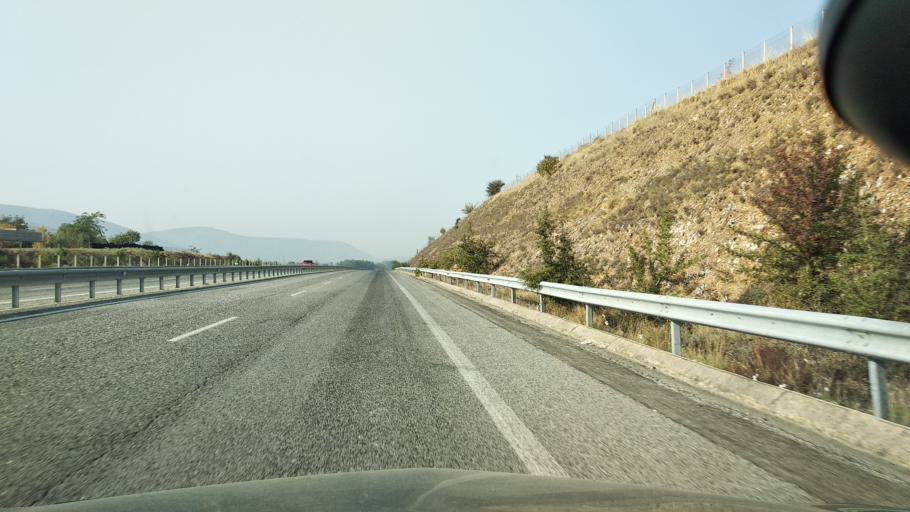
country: GR
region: Thessaly
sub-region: Trikala
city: Zarkos
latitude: 39.5921
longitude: 22.1716
